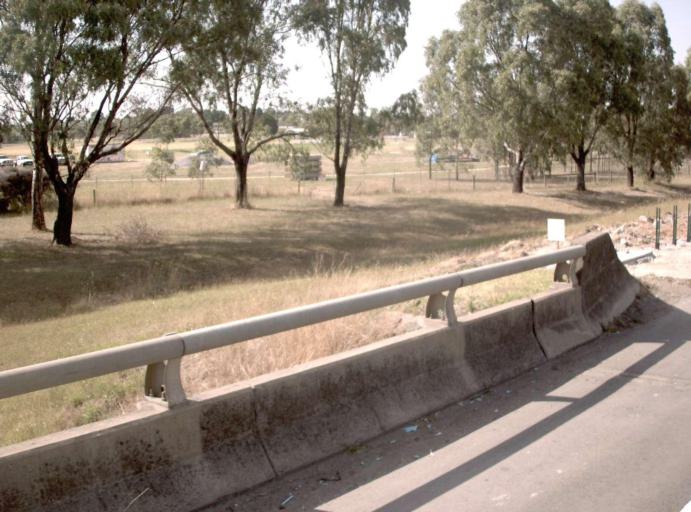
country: AU
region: Victoria
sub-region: Casey
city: Hampton Park
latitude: -38.0192
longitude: 145.2487
